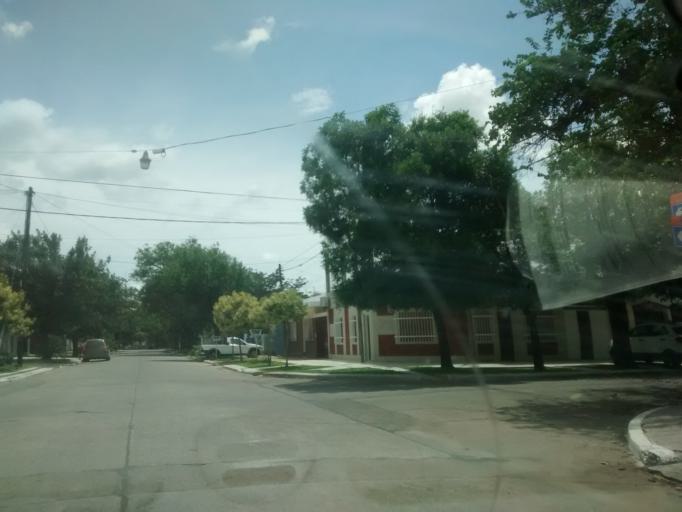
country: AR
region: Chaco
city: Resistencia
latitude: -27.4411
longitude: -58.9875
